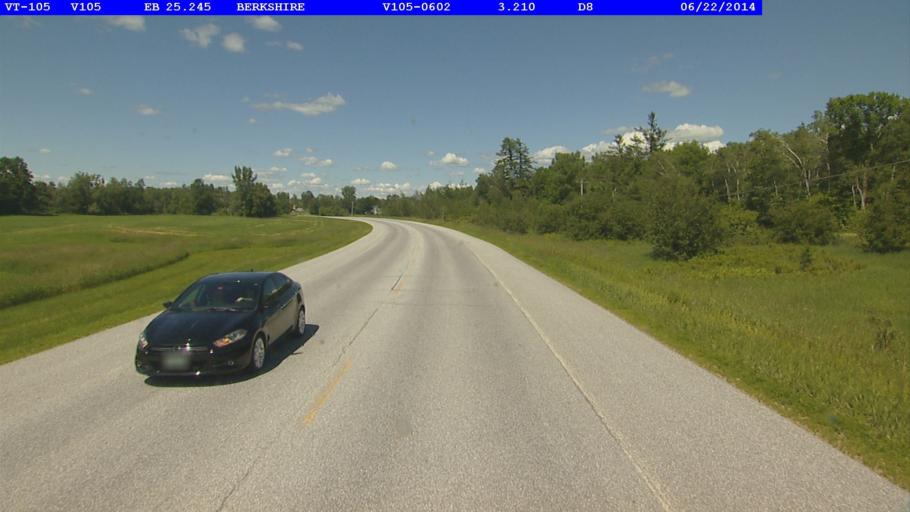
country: US
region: Vermont
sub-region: Franklin County
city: Richford
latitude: 44.9645
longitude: -72.6907
